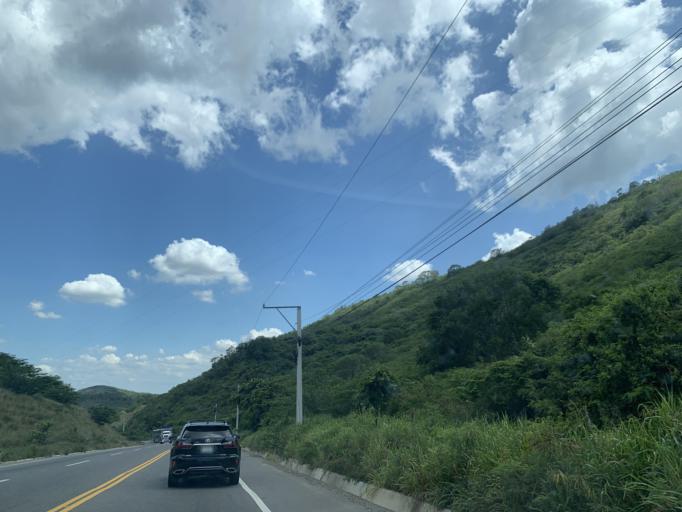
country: DO
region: Santiago
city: Villa Bisono
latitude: 19.6085
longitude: -70.8389
